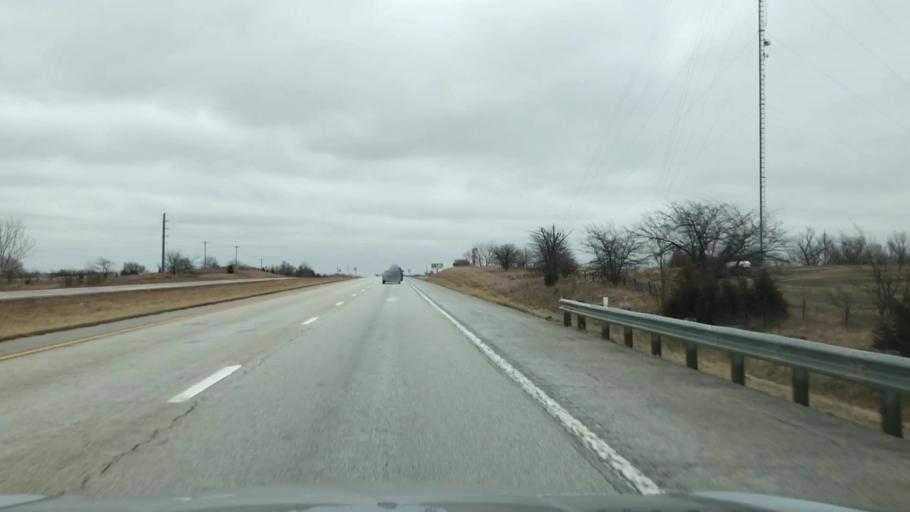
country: US
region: Missouri
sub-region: Clinton County
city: Cameron
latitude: 39.7520
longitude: -94.1893
